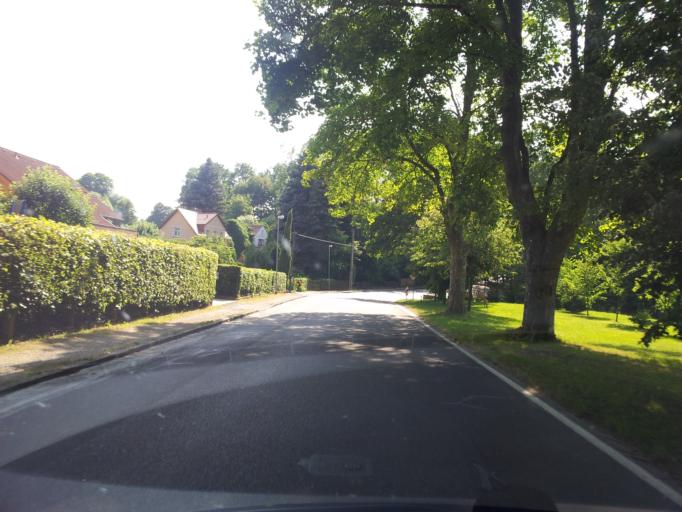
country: DE
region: Saxony
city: Wachau
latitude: 51.1380
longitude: 13.8874
